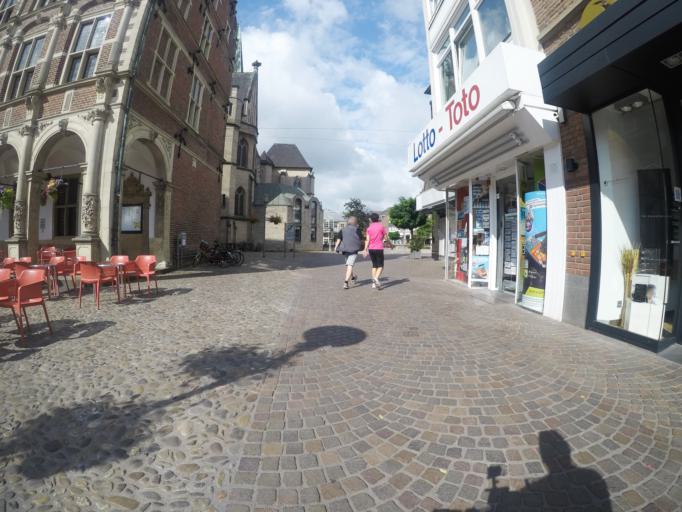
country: DE
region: North Rhine-Westphalia
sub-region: Regierungsbezirk Dusseldorf
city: Bocholt
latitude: 51.8384
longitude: 6.6147
